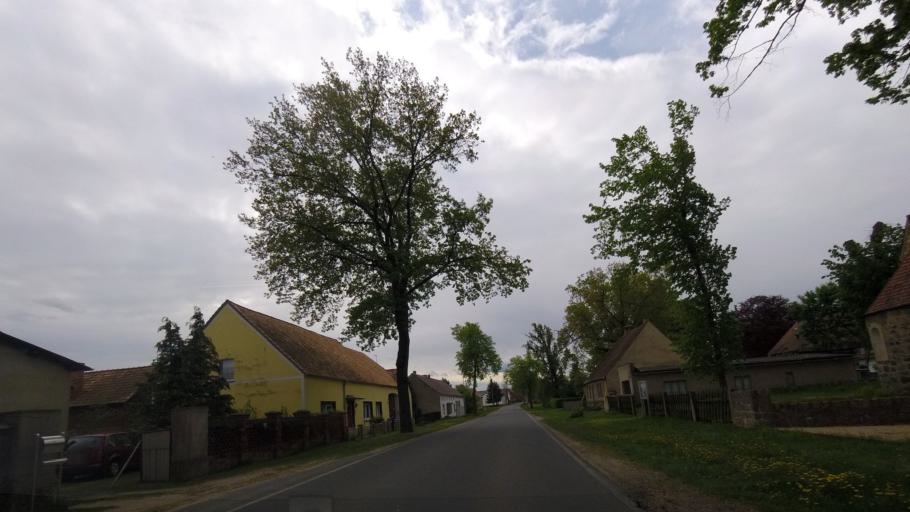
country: DE
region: Brandenburg
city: Dahme
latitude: 51.8981
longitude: 13.4090
